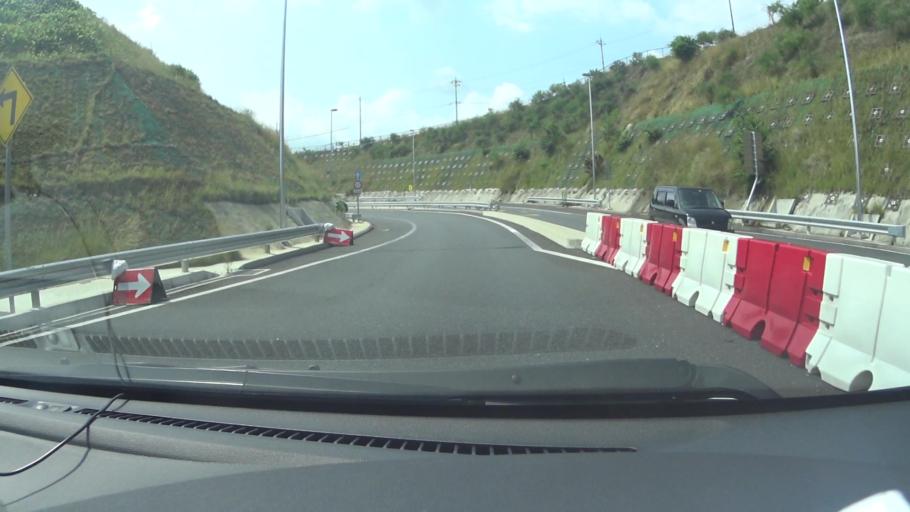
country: JP
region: Kyoto
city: Muko
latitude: 34.9742
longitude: 135.6562
